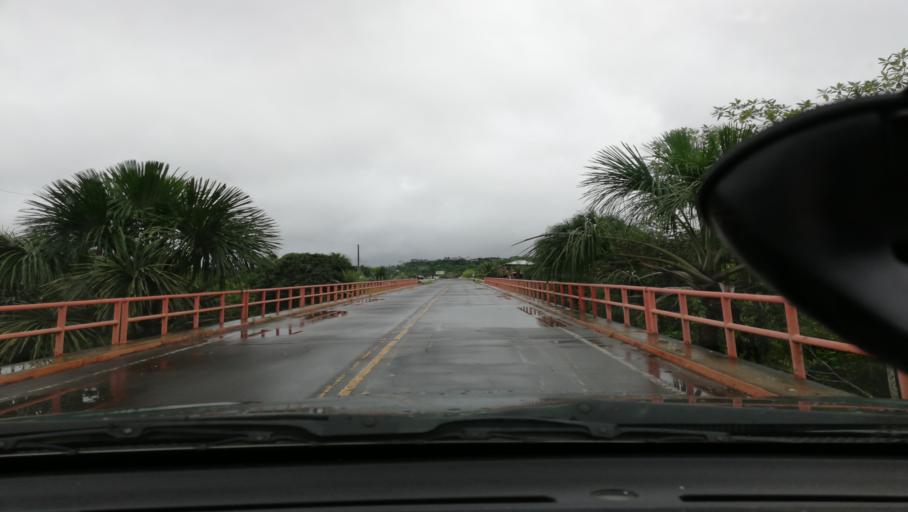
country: PE
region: Loreto
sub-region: Provincia de Loreto
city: Nauta
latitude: -4.2246
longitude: -73.4825
